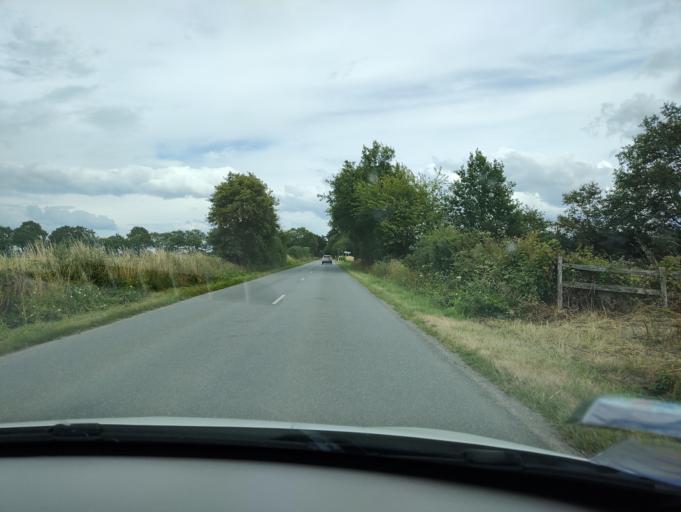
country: FR
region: Pays de la Loire
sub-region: Departement de la Loire-Atlantique
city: Chateaubriant
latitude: 47.7088
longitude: -1.4187
